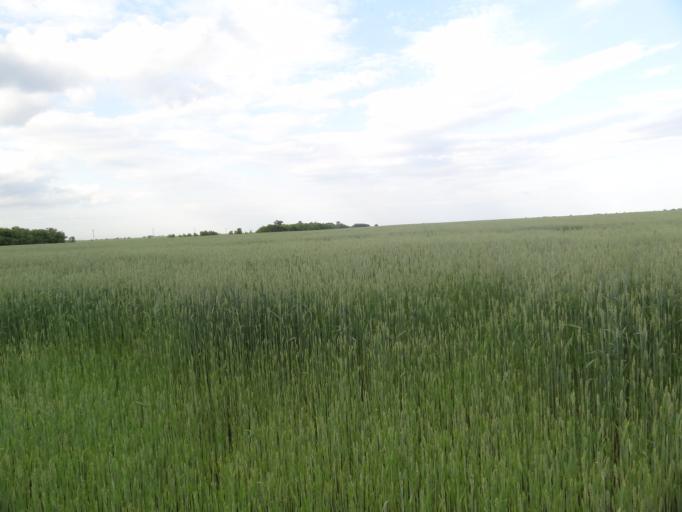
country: RU
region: Saratov
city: Engel's
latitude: 51.4479
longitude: 46.1746
